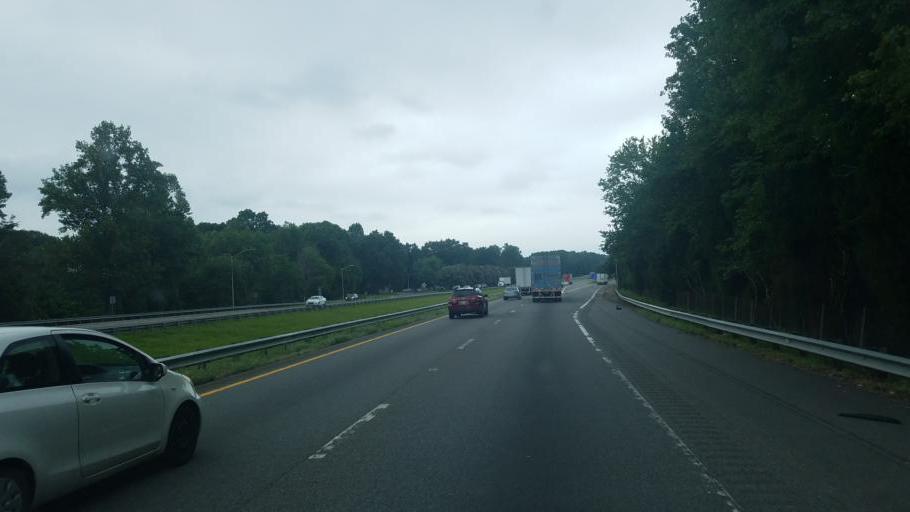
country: US
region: North Carolina
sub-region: Iredell County
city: Mooresville
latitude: 35.6276
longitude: -80.8617
